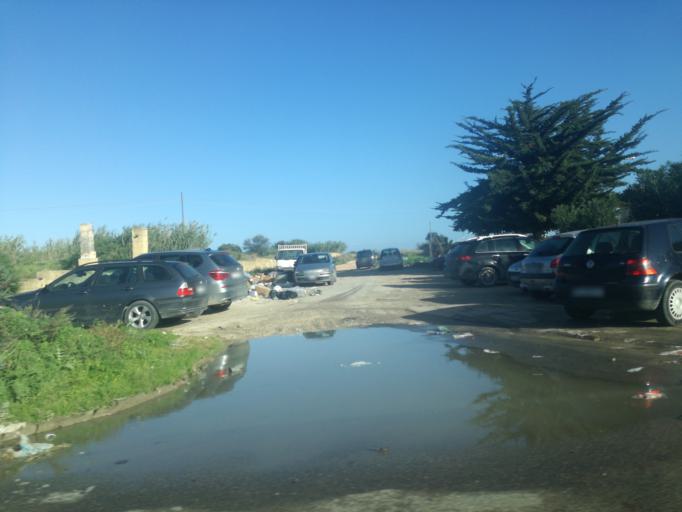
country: IT
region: Sicily
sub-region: Provincia di Caltanissetta
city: Gela
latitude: 37.0581
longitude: 14.2642
